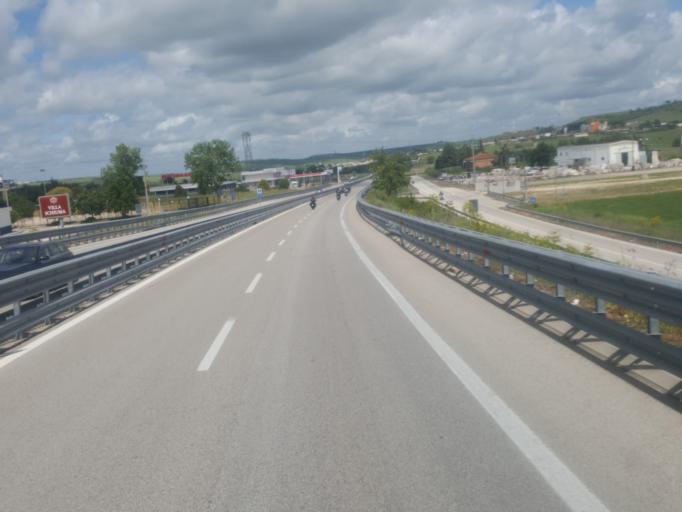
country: IT
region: Basilicate
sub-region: Provincia di Matera
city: Matera
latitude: 40.7081
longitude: 16.5819
